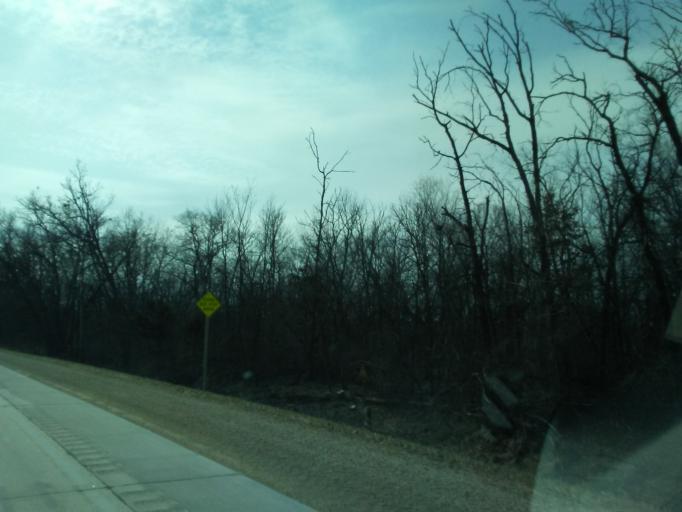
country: US
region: Iowa
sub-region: Winneshiek County
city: Decorah
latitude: 43.3422
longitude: -91.8102
